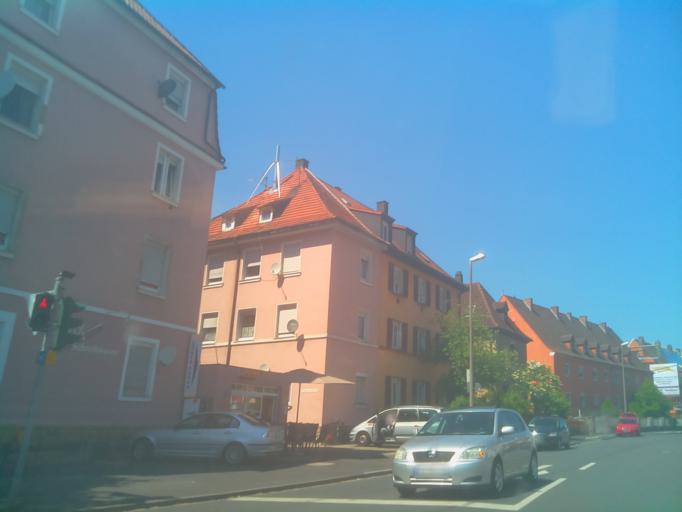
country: DE
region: Bavaria
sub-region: Regierungsbezirk Unterfranken
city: Schweinfurt
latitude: 50.0477
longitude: 10.2193
